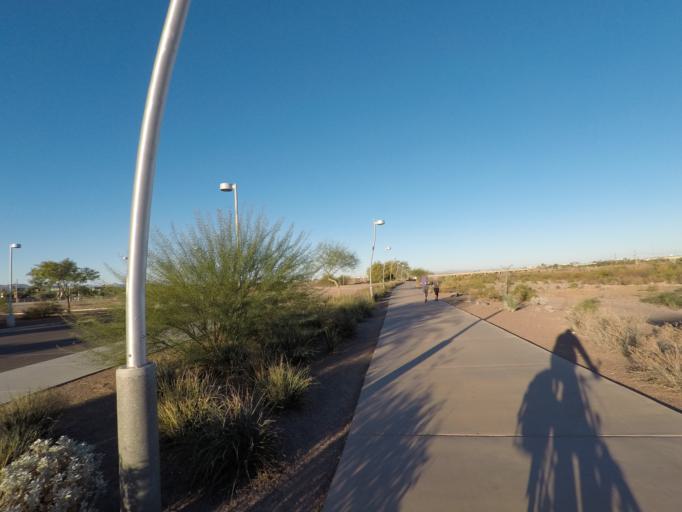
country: US
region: Arizona
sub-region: Maricopa County
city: Tempe Junction
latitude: 33.4325
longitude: -111.9507
